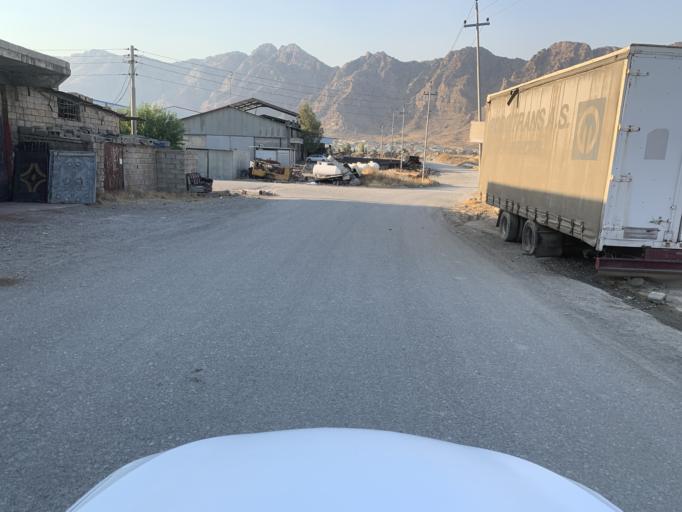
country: IQ
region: As Sulaymaniyah
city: Raniye
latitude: 36.2467
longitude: 44.8892
